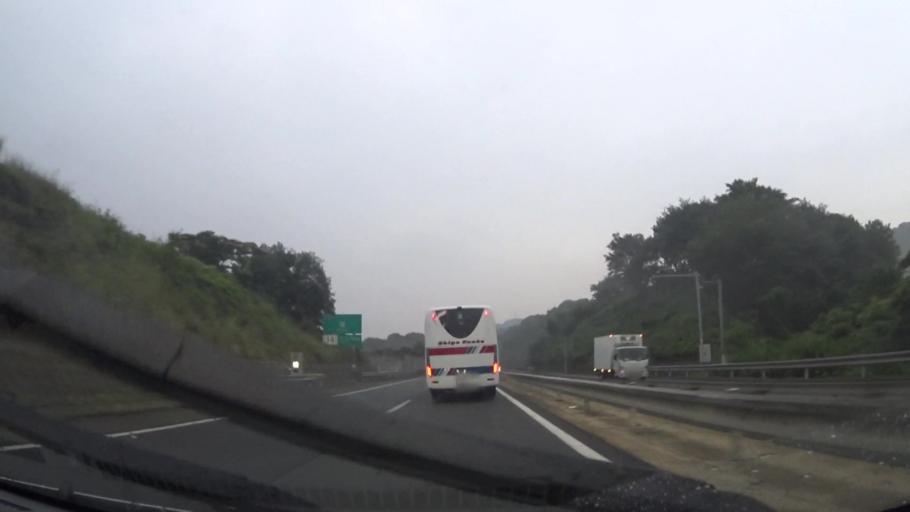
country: JP
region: Kyoto
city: Kameoka
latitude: 34.9902
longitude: 135.5925
